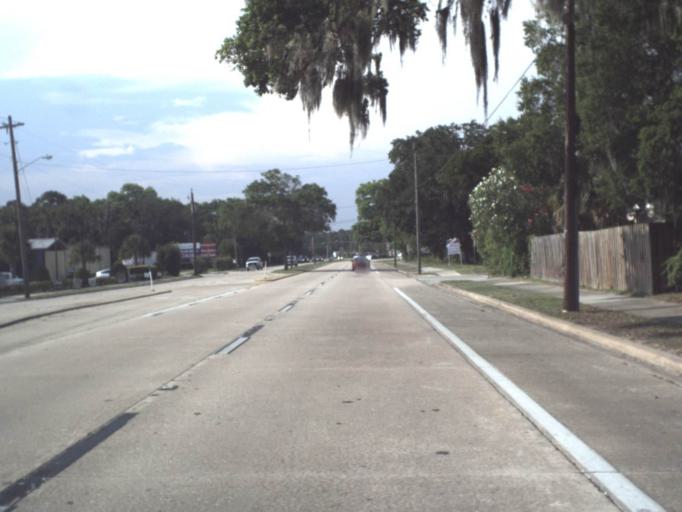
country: US
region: Florida
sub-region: Saint Johns County
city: Saint Augustine
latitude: 29.9196
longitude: -81.3248
